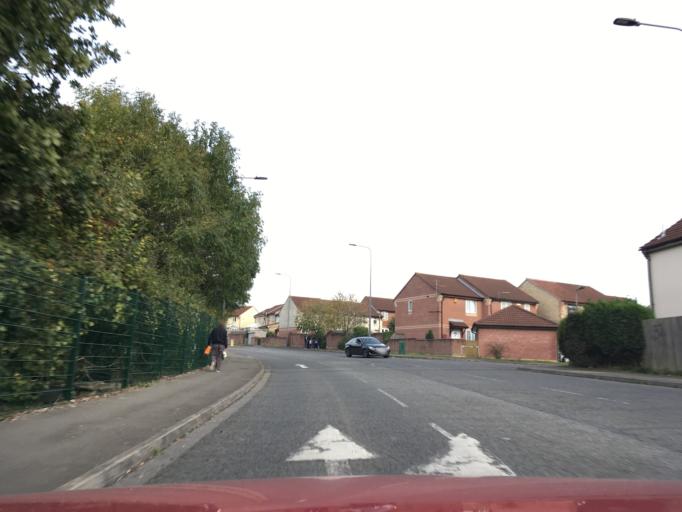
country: GB
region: England
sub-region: South Gloucestershire
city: Stoke Gifford
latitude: 51.5240
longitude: -2.5379
